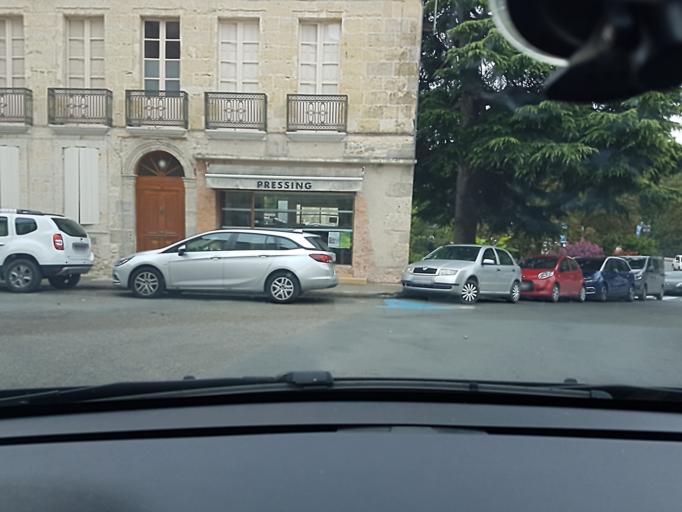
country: FR
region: Aquitaine
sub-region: Departement du Lot-et-Garonne
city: Nerac
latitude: 44.1355
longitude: 0.3405
